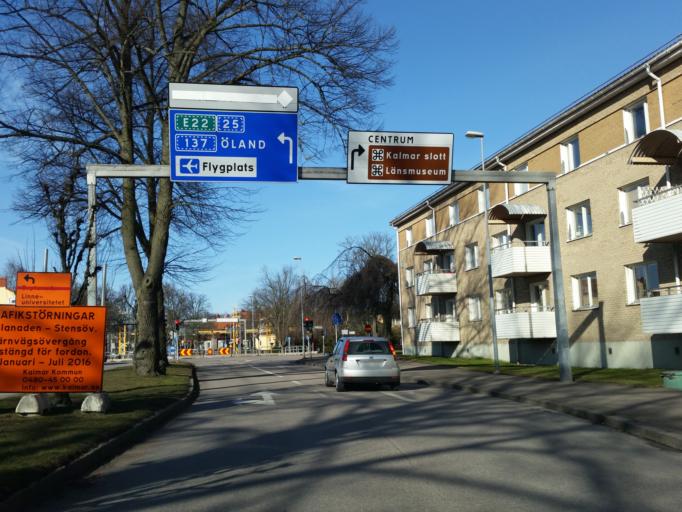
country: SE
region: Kalmar
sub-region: Kalmar Kommun
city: Kalmar
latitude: 56.6625
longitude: 16.3469
